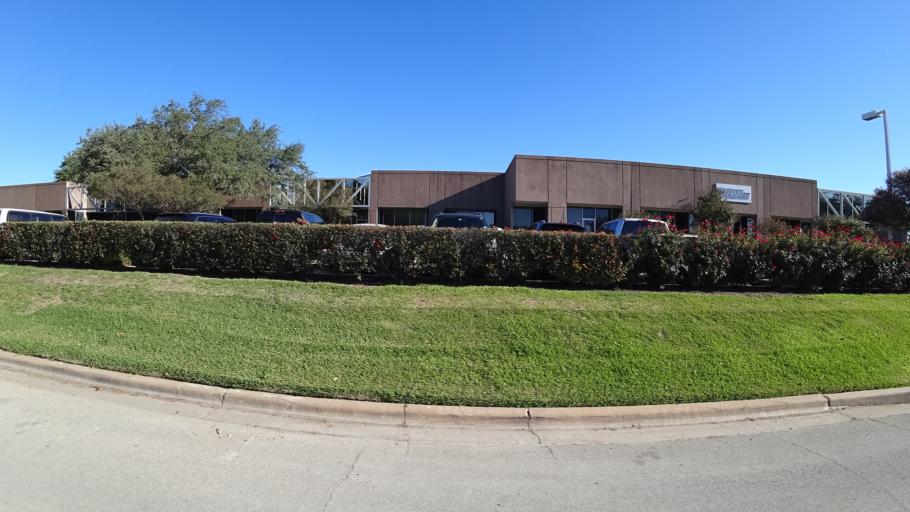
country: US
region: Texas
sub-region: Travis County
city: Manor
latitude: 30.3244
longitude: -97.6567
